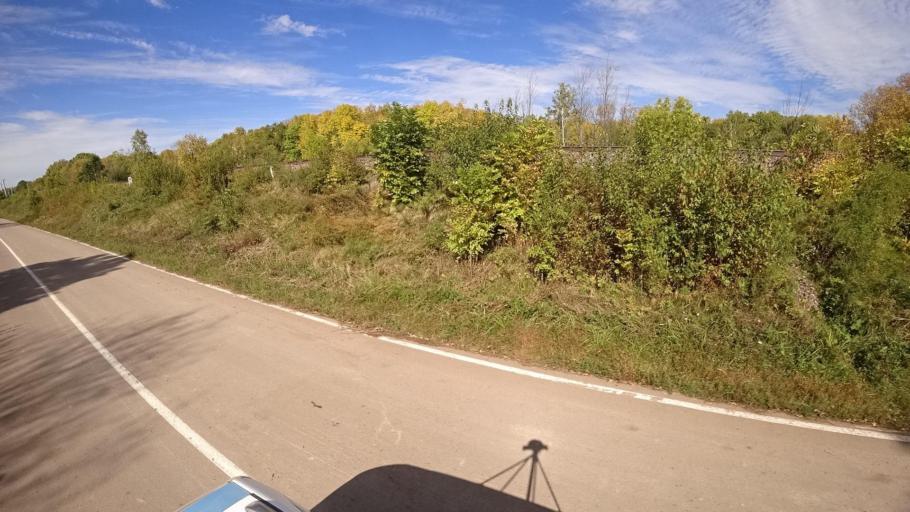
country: RU
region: Primorskiy
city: Yakovlevka
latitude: 44.3927
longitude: 133.6078
